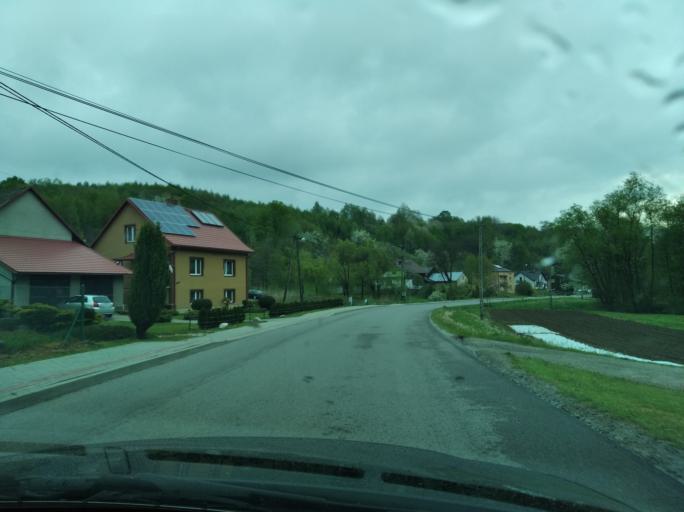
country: PL
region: Subcarpathian Voivodeship
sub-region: Powiat rzeszowski
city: Lecka
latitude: 49.8778
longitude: 22.0160
